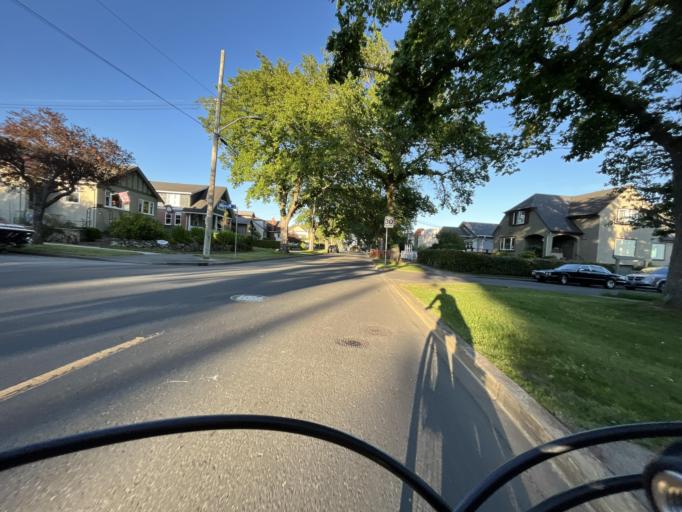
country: CA
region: British Columbia
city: Victoria
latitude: 48.4089
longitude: -123.3341
